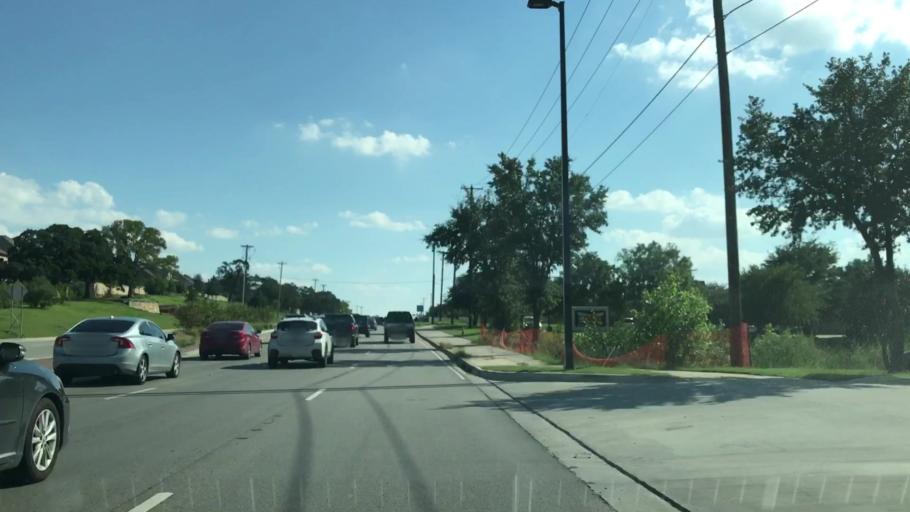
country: US
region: Texas
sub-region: Tarrant County
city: Southlake
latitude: 32.9367
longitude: -97.1859
